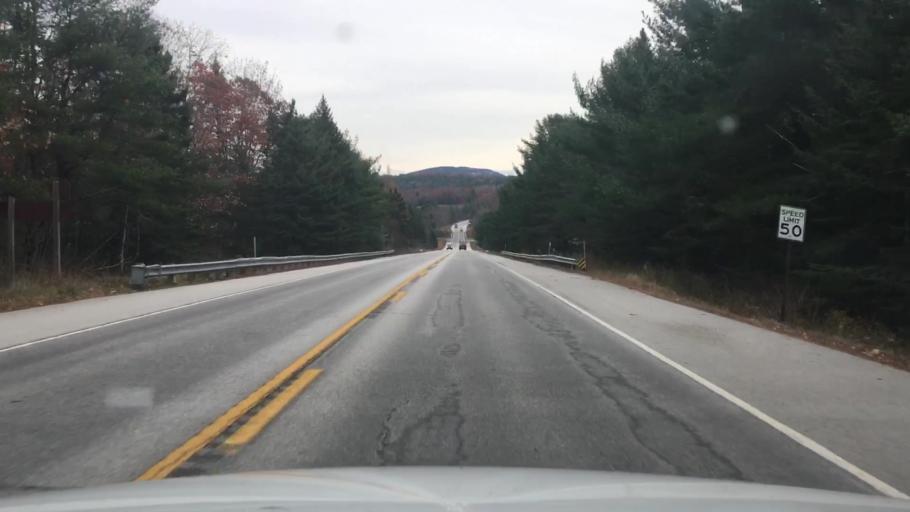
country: US
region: Maine
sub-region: Hancock County
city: Orland
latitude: 44.5734
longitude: -68.7515
